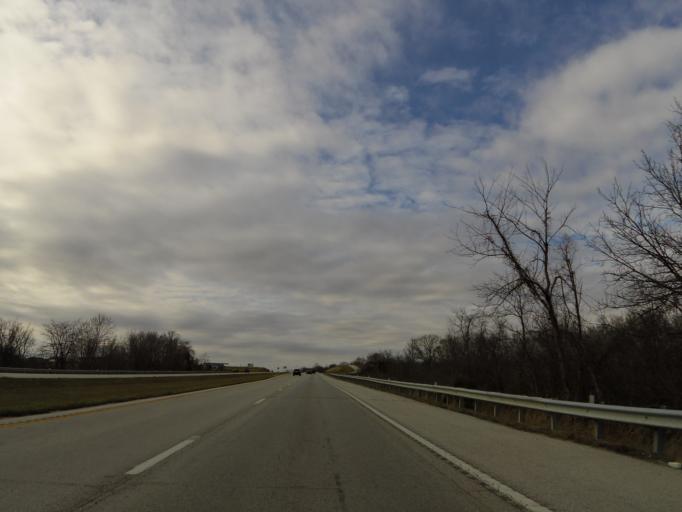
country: US
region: Missouri
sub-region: Marion County
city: Hannibal
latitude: 39.7396
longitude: -91.4158
